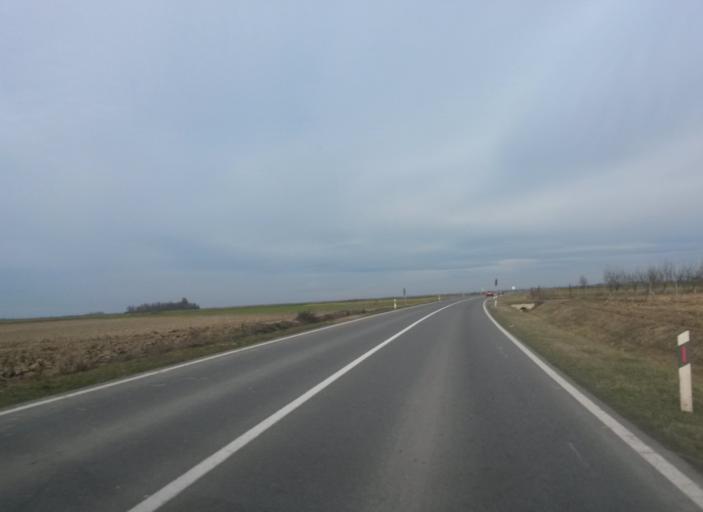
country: HR
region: Osjecko-Baranjska
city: Cepin
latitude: 45.5197
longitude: 18.5372
